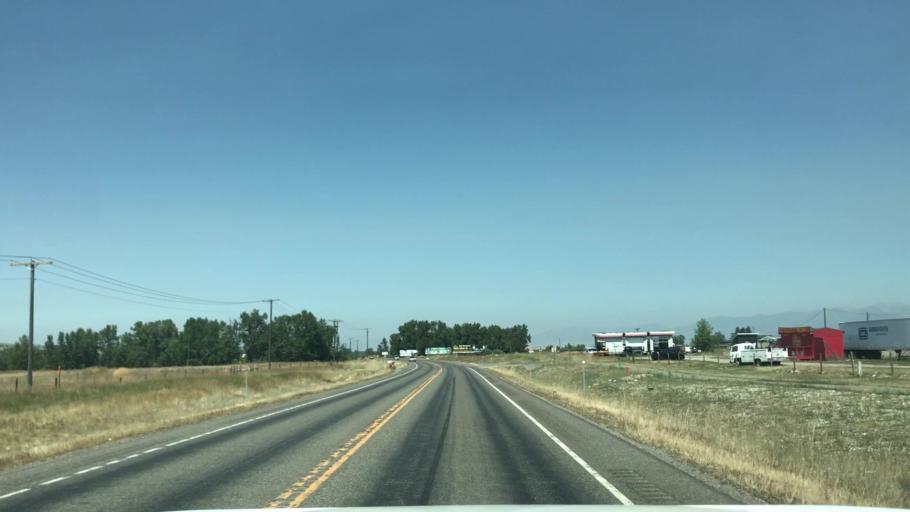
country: US
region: Montana
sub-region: Gallatin County
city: Four Corners
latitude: 45.6061
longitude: -111.1958
